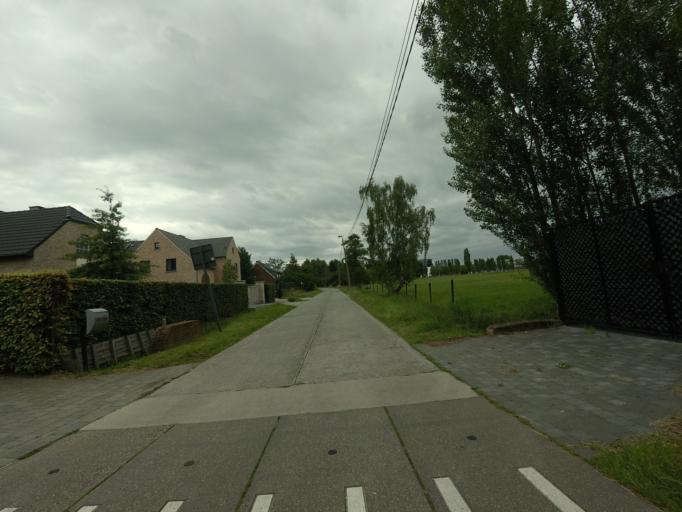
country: BE
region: Flanders
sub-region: Provincie Antwerpen
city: Lier
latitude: 51.1082
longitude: 4.5428
